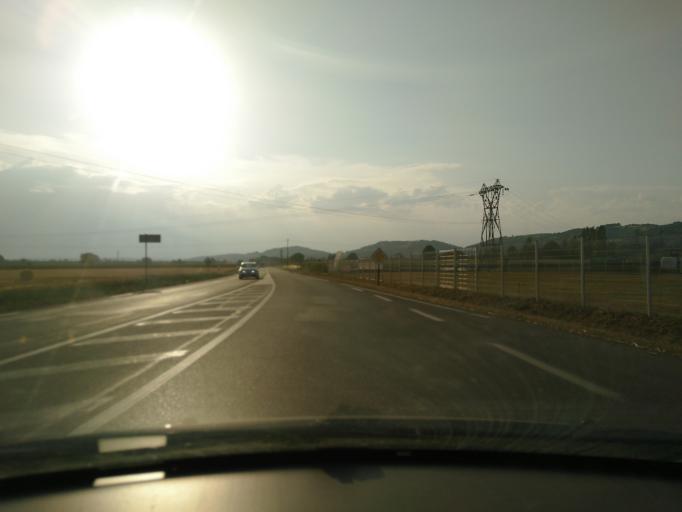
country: FR
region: Rhone-Alpes
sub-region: Departement de l'Isere
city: La Cote-Saint-Andre
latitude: 45.3806
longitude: 5.2617
